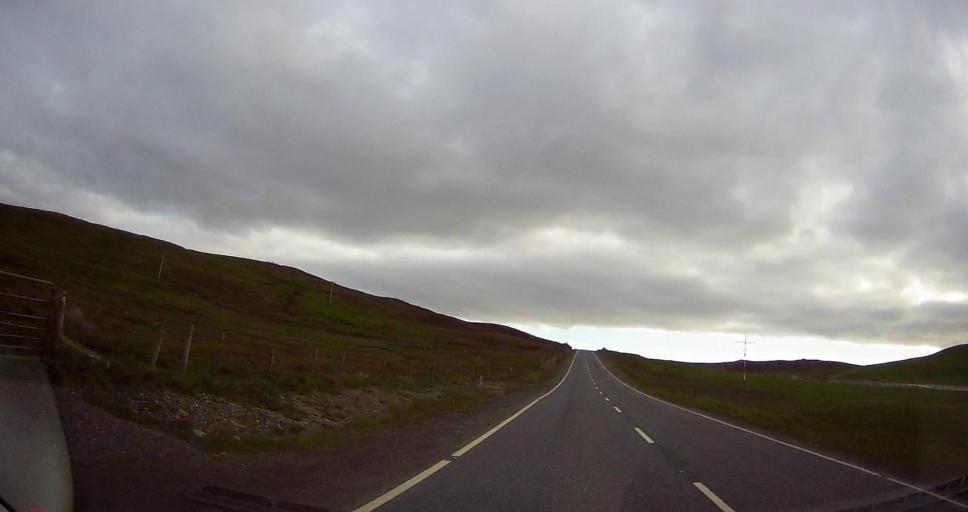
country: GB
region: Scotland
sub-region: Shetland Islands
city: Lerwick
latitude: 60.4299
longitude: -1.3009
